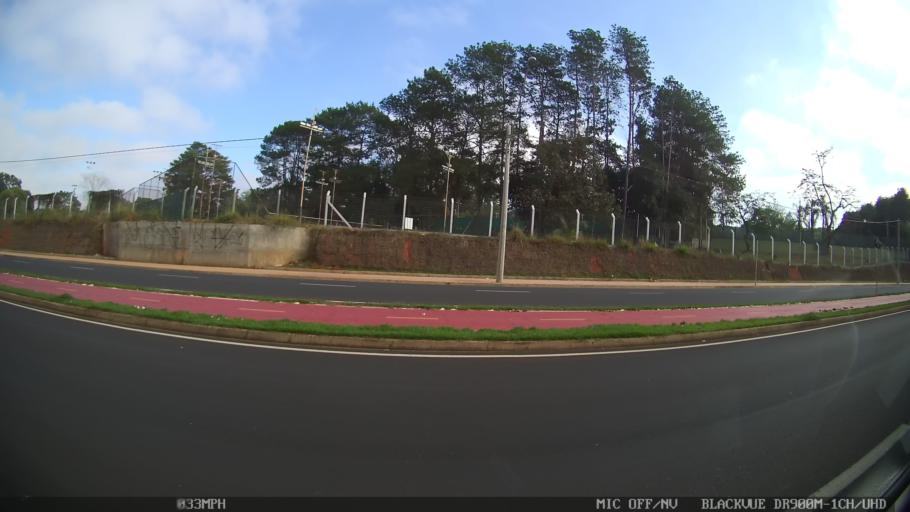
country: BR
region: Sao Paulo
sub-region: Sao Jose Do Rio Preto
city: Sao Jose do Rio Preto
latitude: -20.8107
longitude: -49.4321
